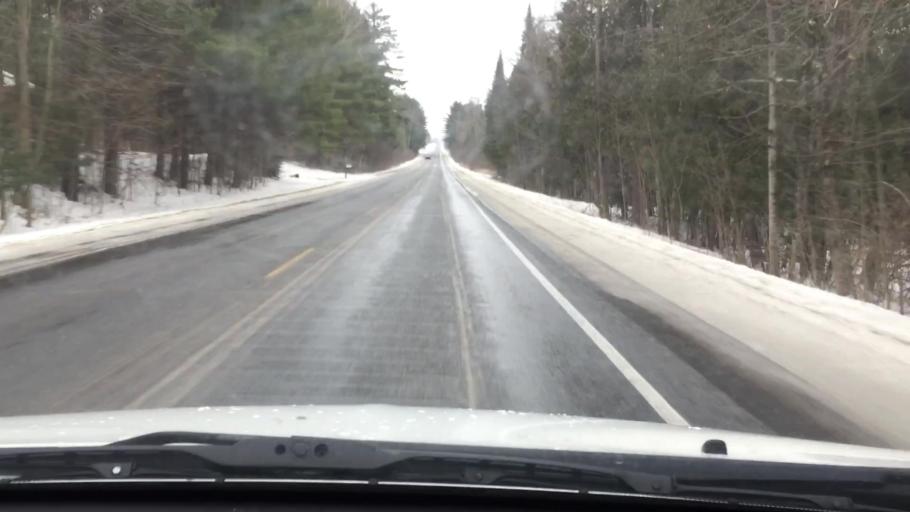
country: US
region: Michigan
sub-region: Osceola County
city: Reed City
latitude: 44.0576
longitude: -85.4440
